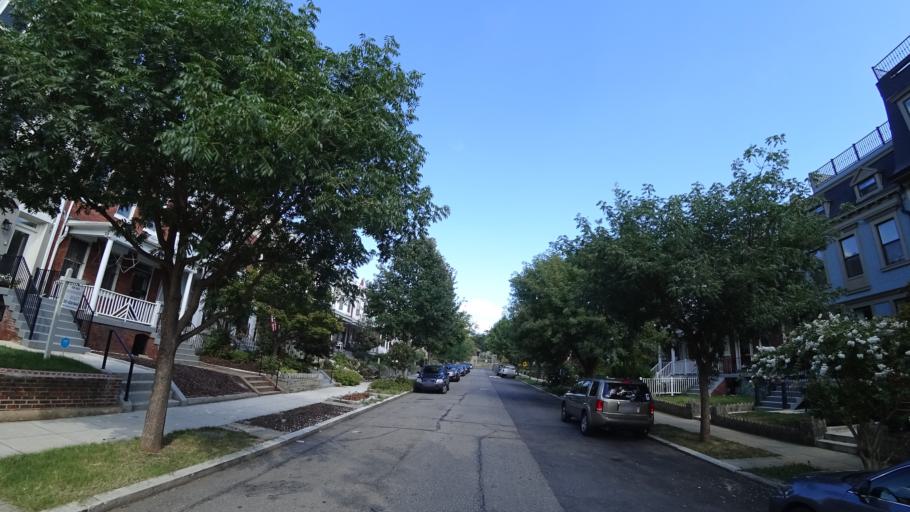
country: US
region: Washington, D.C.
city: Washington, D.C.
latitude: 38.9191
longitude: -77.0105
